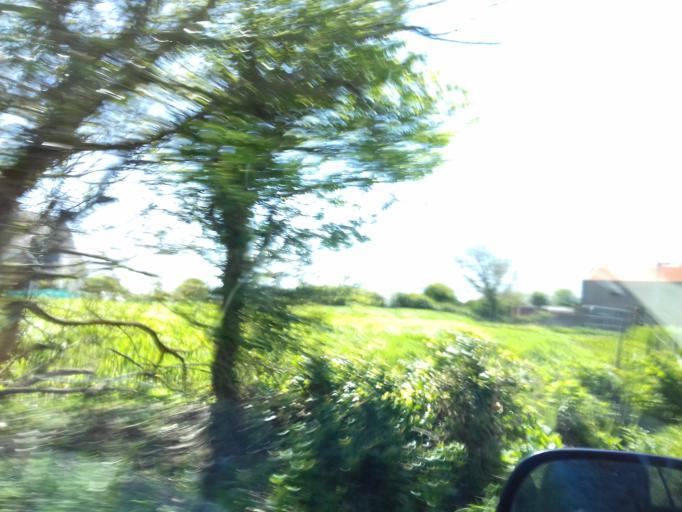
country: IE
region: Munster
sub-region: Waterford
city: Dunmore East
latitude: 52.1761
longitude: -6.8782
